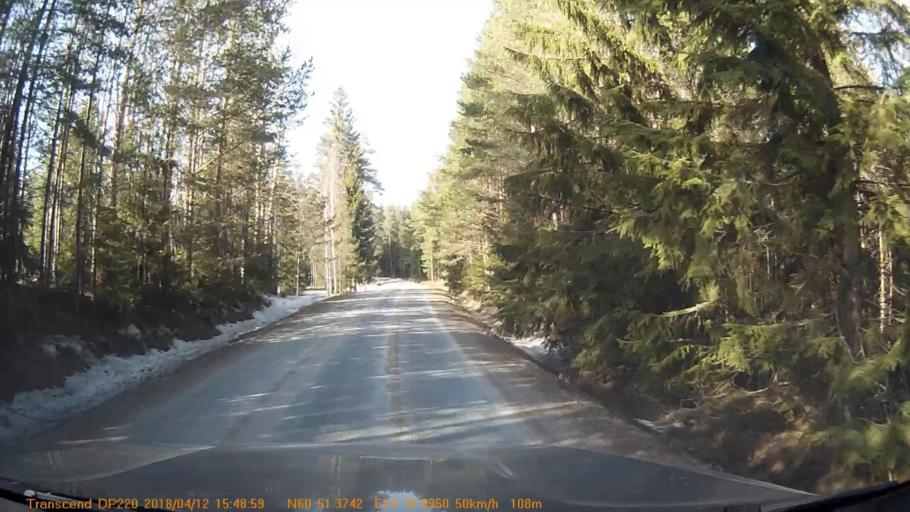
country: FI
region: Haeme
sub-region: Forssa
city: Forssa
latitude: 60.8564
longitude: 23.5499
